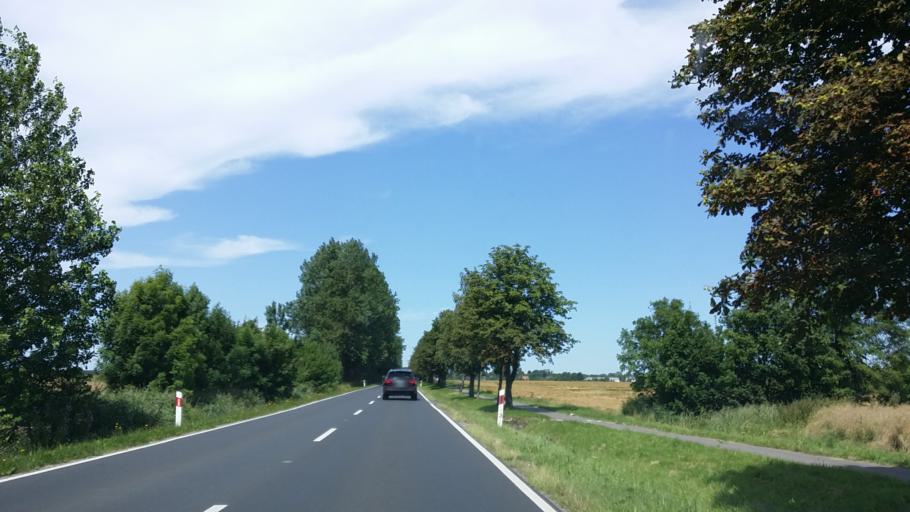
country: PL
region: West Pomeranian Voivodeship
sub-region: Powiat koszalinski
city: Mielno
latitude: 54.2297
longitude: 16.0750
